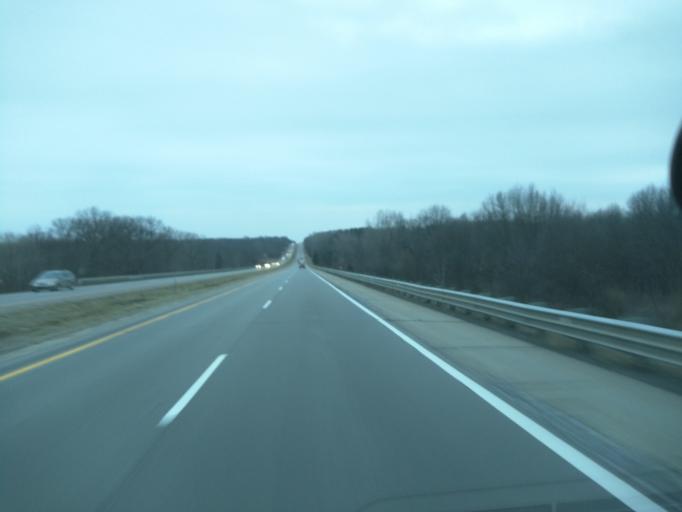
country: US
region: Michigan
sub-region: Ingham County
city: Leslie
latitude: 42.4096
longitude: -84.4293
